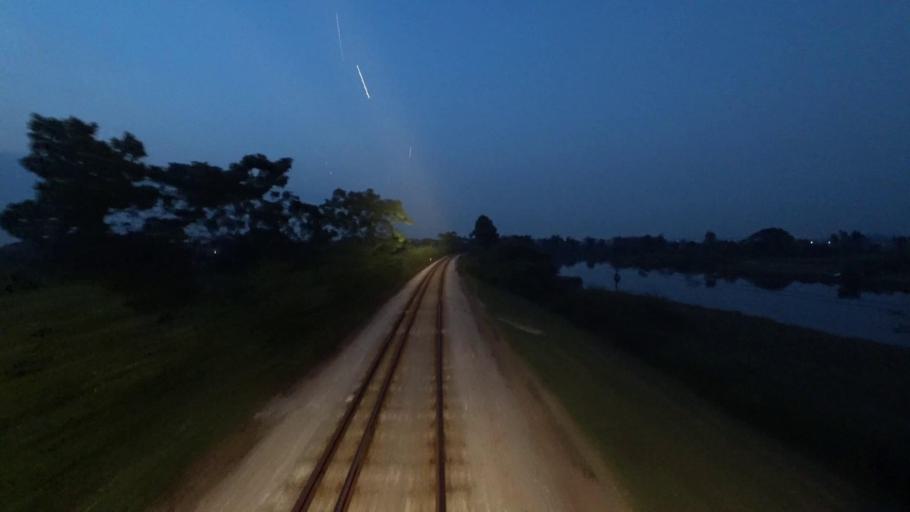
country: VN
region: Ha Noi
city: Soc Son
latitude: 21.2762
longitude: 105.8626
